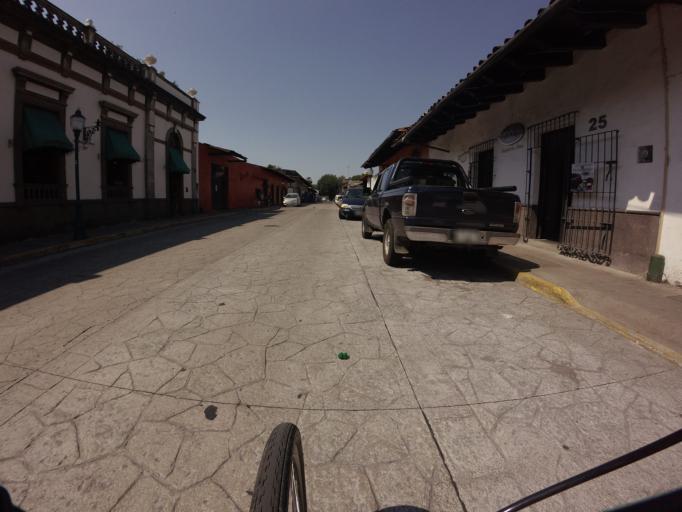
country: MX
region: Veracruz
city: Coatepec
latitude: 19.4561
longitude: -96.9580
